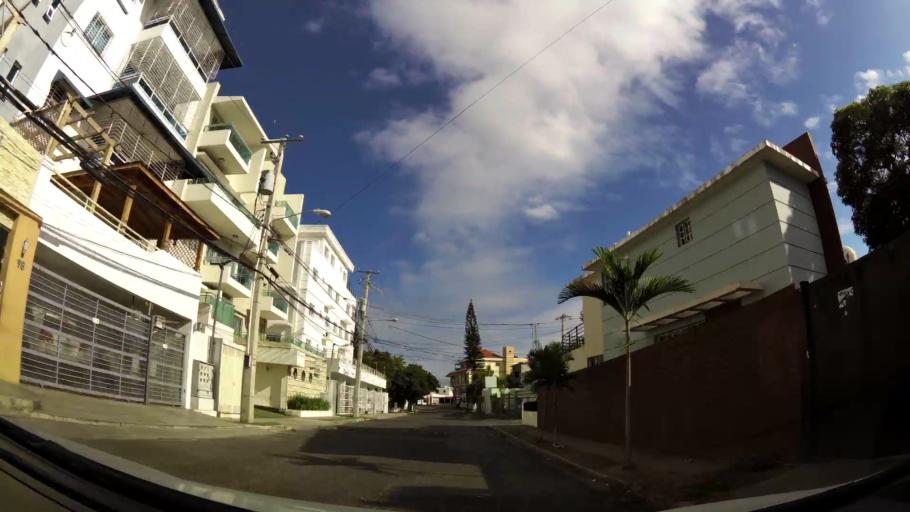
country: DO
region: Nacional
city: Bella Vista
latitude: 18.4651
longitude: -69.9540
